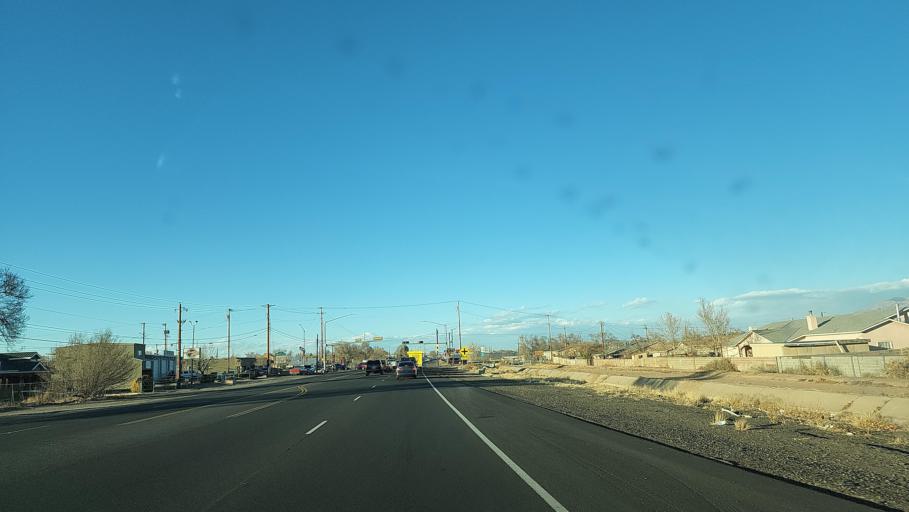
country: US
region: New Mexico
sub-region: Bernalillo County
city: South Valley
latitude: 35.0291
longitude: -106.7137
